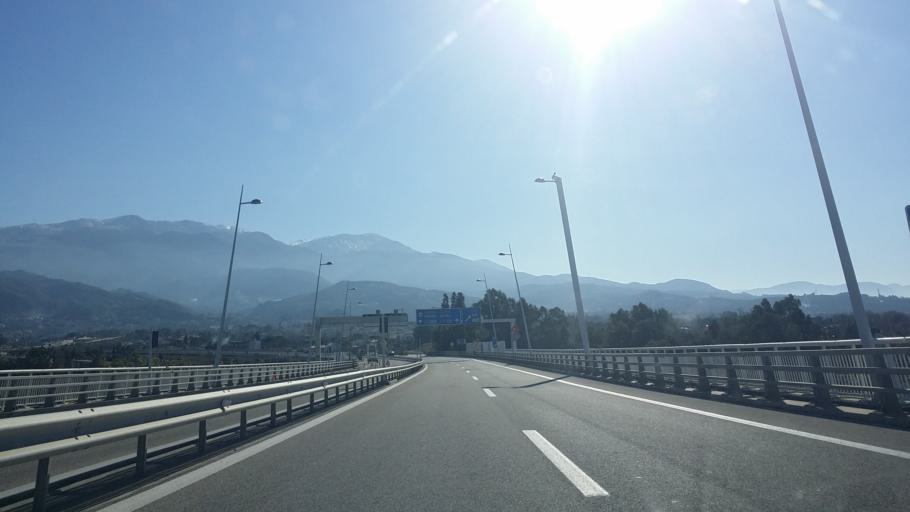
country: GR
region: West Greece
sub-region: Nomos Achaias
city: Rio
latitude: 38.3090
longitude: 21.7795
